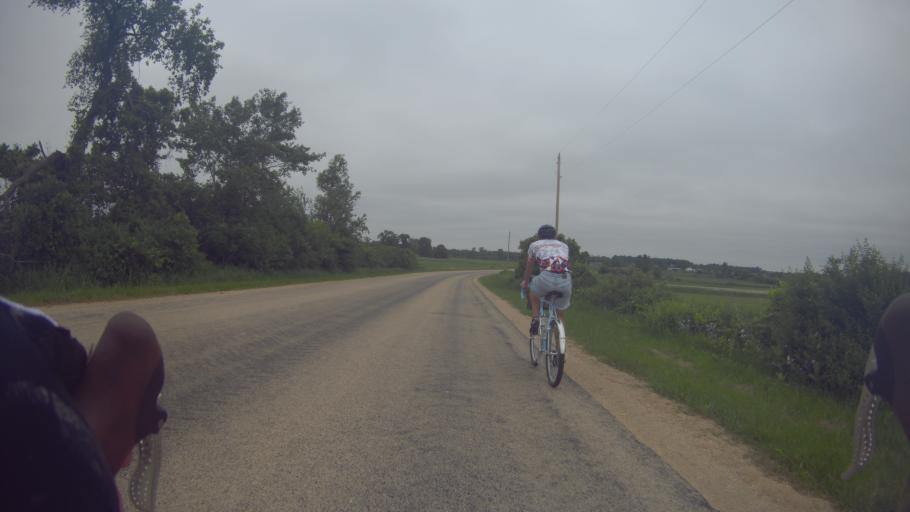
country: US
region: Wisconsin
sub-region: Green County
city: Brooklyn
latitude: 42.8502
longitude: -89.4141
